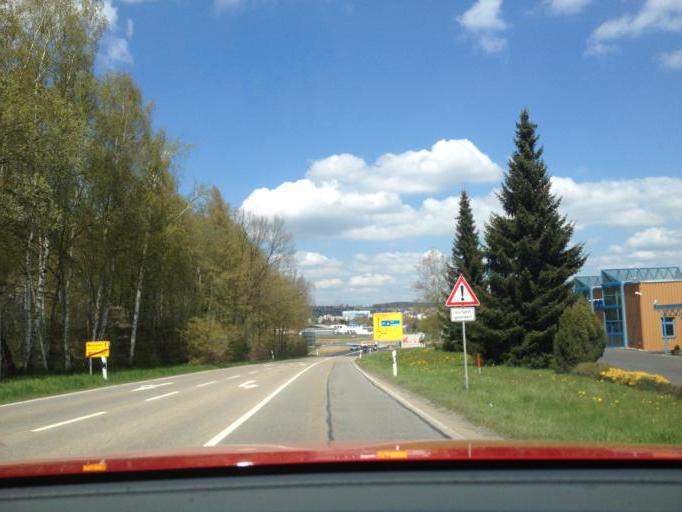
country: DE
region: Bavaria
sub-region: Upper Palatinate
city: Waldershof
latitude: 49.9848
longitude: 12.0680
